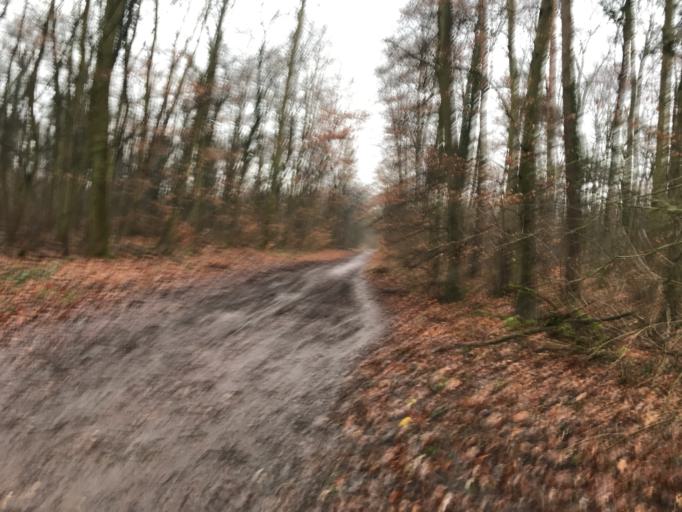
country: DE
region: Rheinland-Pfalz
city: Budenheim
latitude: 50.0154
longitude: 8.1817
